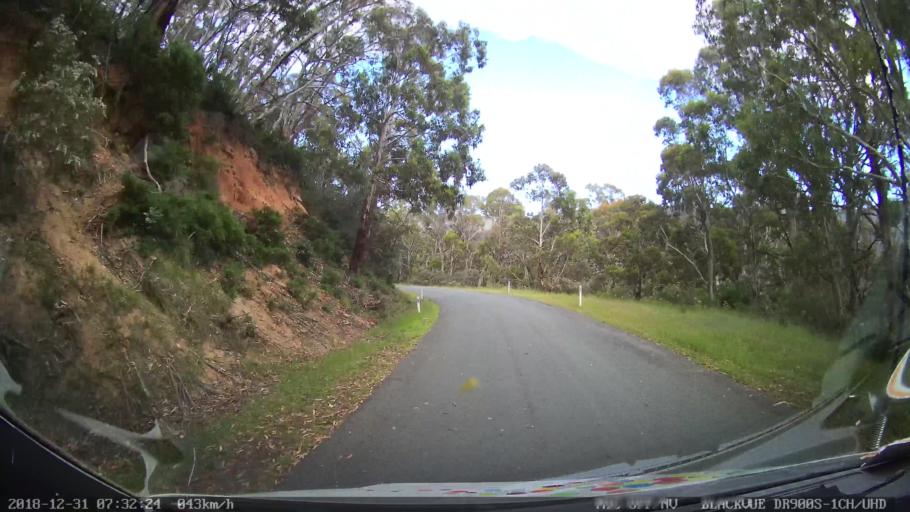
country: AU
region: New South Wales
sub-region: Snowy River
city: Jindabyne
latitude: -36.3303
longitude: 148.4656
